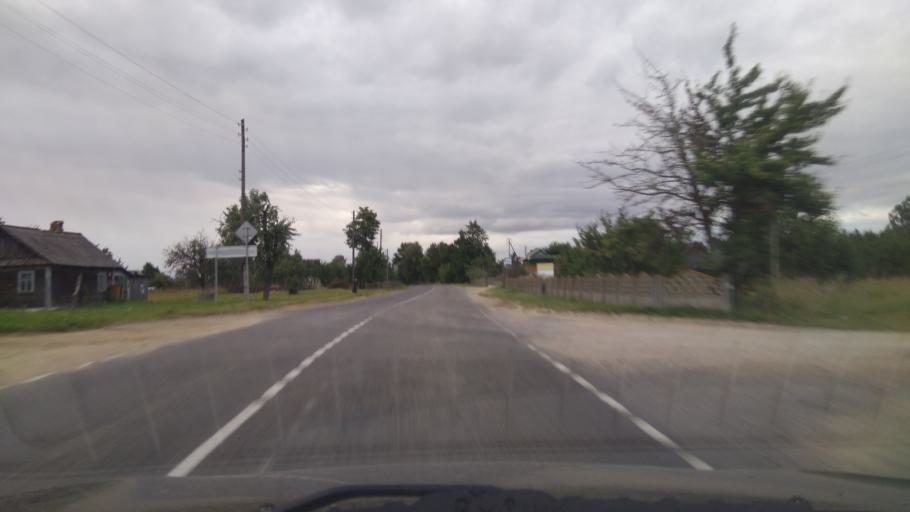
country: BY
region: Brest
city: Byaroza
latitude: 52.4218
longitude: 24.9809
